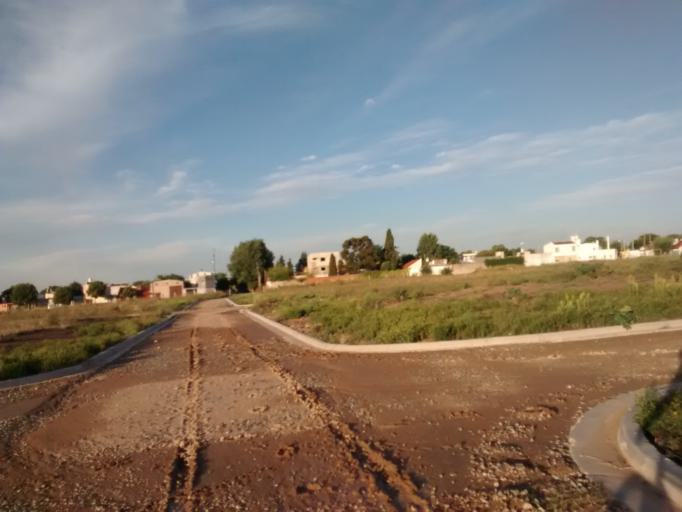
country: AR
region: Buenos Aires
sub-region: Partido de La Plata
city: La Plata
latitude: -34.9528
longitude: -57.9385
